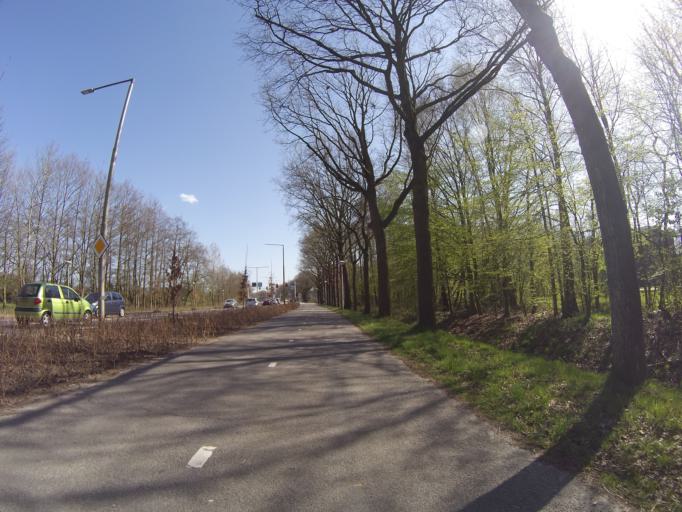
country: NL
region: Utrecht
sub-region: Gemeente Amersfoort
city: Hoogland
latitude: 52.1728
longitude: 5.3704
